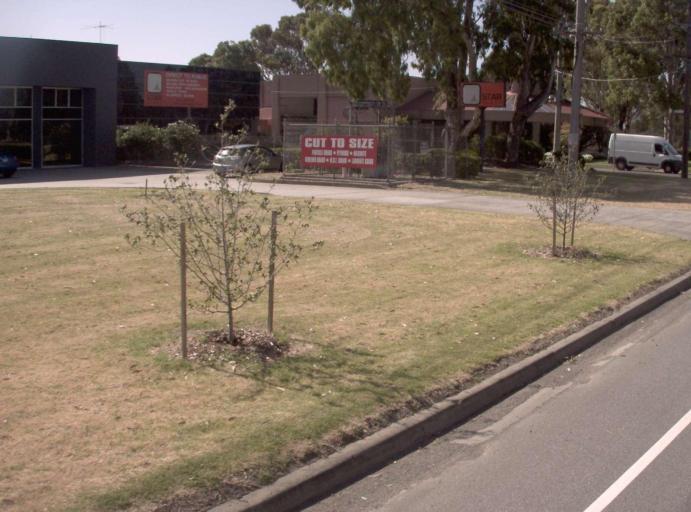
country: AU
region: Victoria
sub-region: Casey
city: Hampton Park
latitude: -38.0227
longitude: 145.2136
